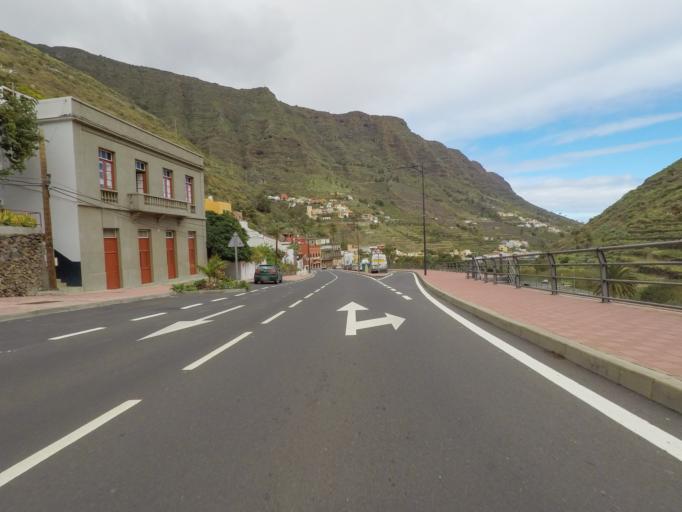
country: ES
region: Canary Islands
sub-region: Provincia de Santa Cruz de Tenerife
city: Hermigua
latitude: 28.1619
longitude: -17.1982
